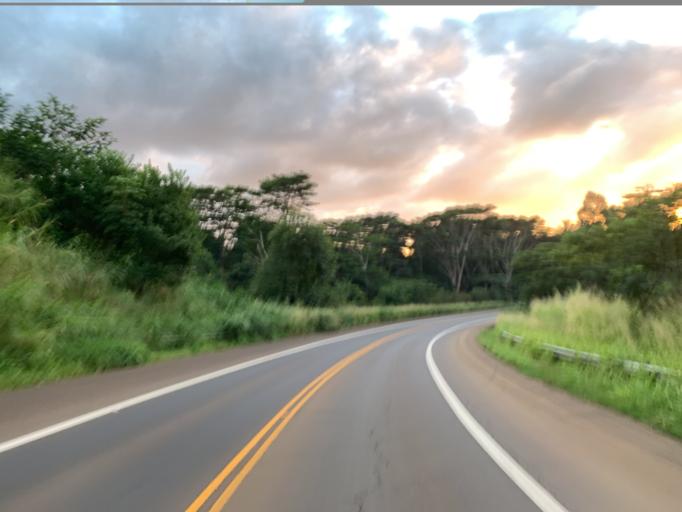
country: US
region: Hawaii
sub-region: Maui County
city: Haiku-Pauwela
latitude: 20.9194
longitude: -156.2956
